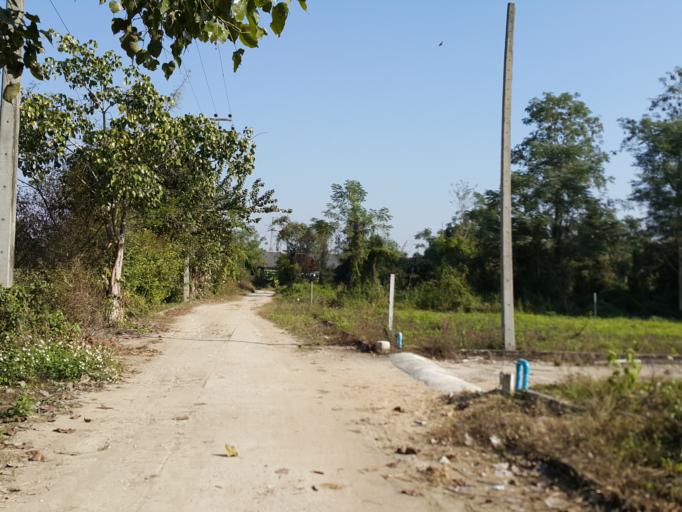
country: TH
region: Chiang Mai
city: San Kamphaeng
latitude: 18.8080
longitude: 99.1102
